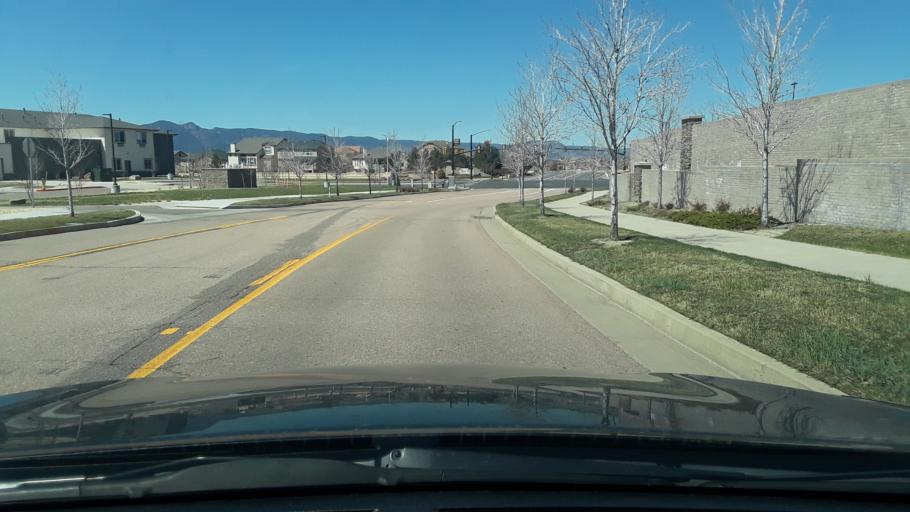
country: US
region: Colorado
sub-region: El Paso County
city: Black Forest
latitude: 38.9702
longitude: -104.7503
